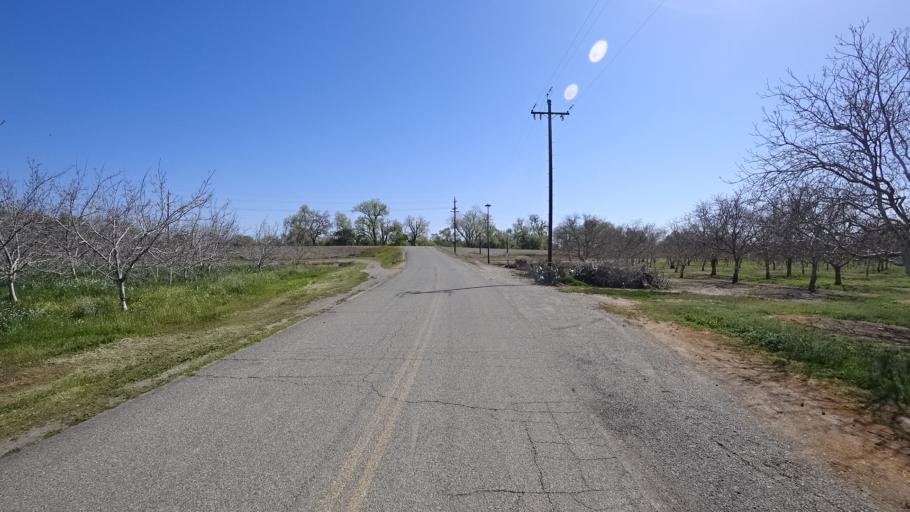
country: US
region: California
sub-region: Glenn County
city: Willows
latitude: 39.4428
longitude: -122.0156
